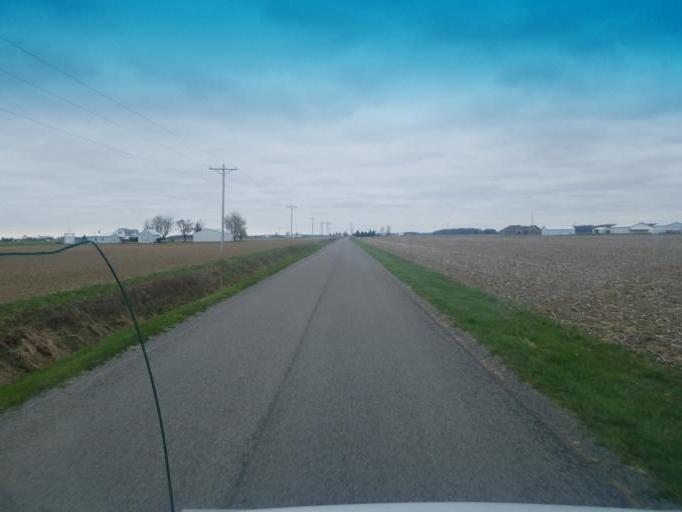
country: US
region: Ohio
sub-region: Allen County
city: Delphos
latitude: 40.9221
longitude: -84.3797
